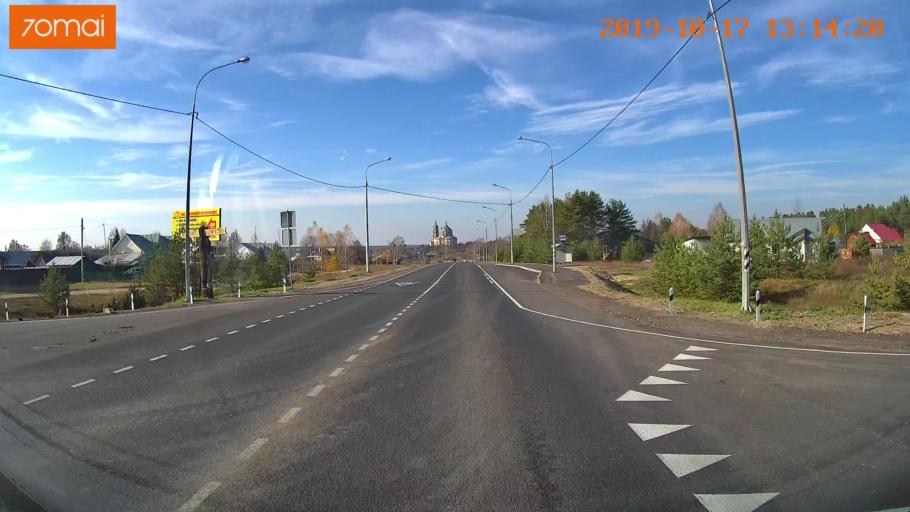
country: RU
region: Rjazan
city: Gus'-Zheleznyy
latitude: 55.0517
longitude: 41.1731
